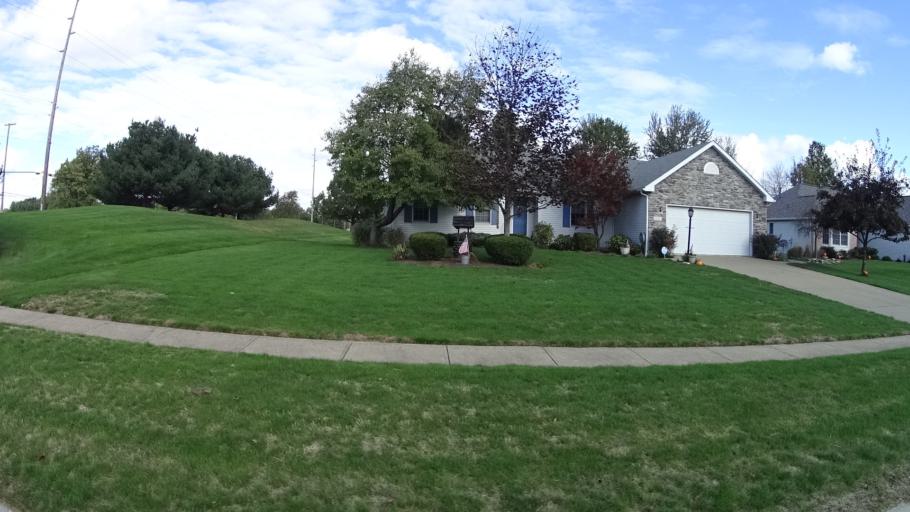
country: US
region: Ohio
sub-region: Lorain County
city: Grafton
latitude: 41.2892
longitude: -82.0651
